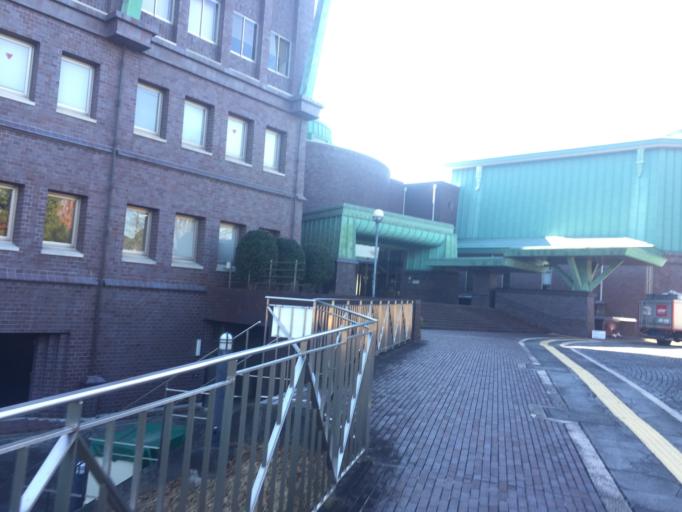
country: JP
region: Shizuoka
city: Kakegawa
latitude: 34.7874
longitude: 137.9702
